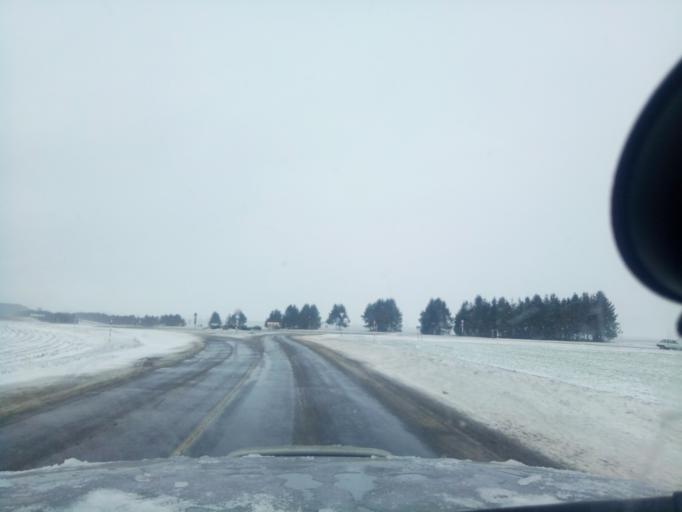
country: BY
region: Minsk
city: Haradzyeya
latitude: 53.2950
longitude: 26.5752
